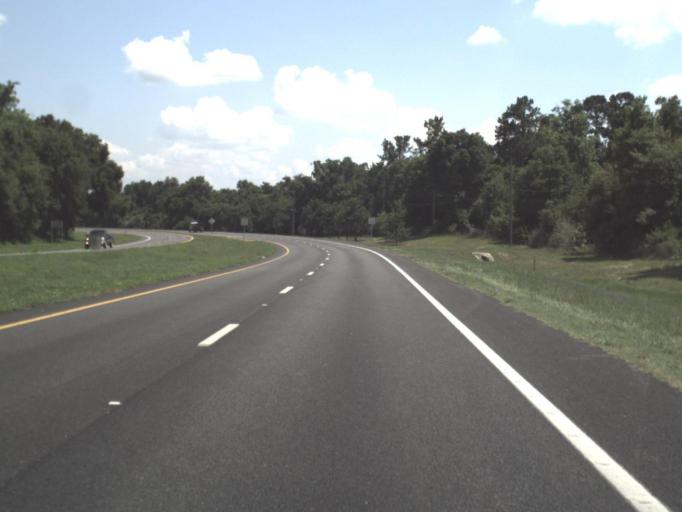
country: US
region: Florida
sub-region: Alachua County
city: Gainesville
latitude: 29.6169
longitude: -82.2558
